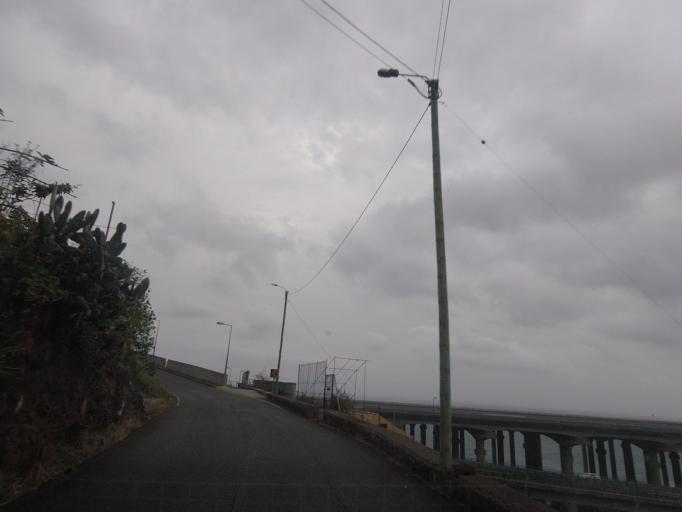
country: PT
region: Madeira
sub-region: Machico
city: Machico
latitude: 32.7042
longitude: -16.7709
